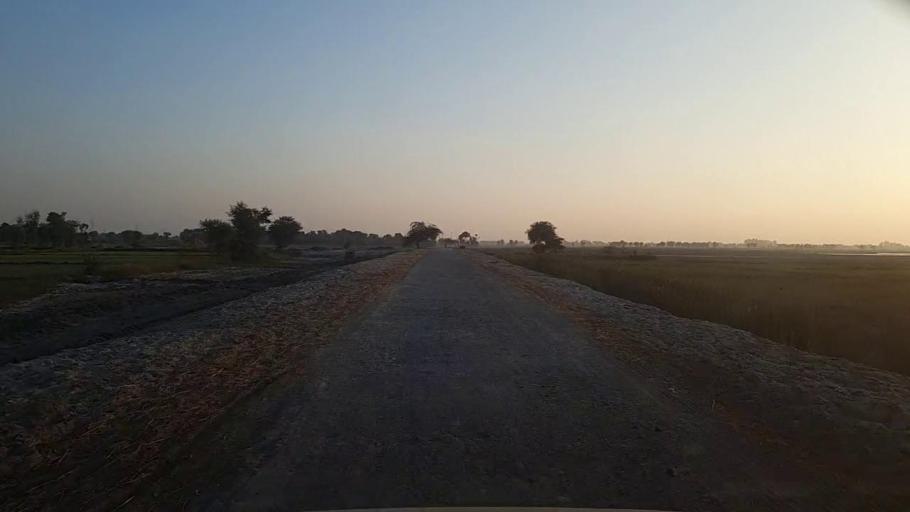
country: PK
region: Sindh
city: Khairpur Nathan Shah
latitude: 27.1753
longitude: 67.7339
